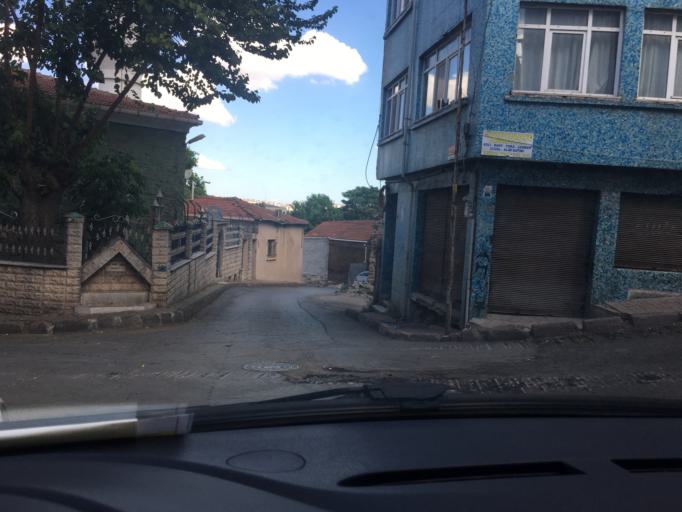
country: TR
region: Istanbul
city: Eminoenue
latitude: 41.0186
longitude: 28.9619
